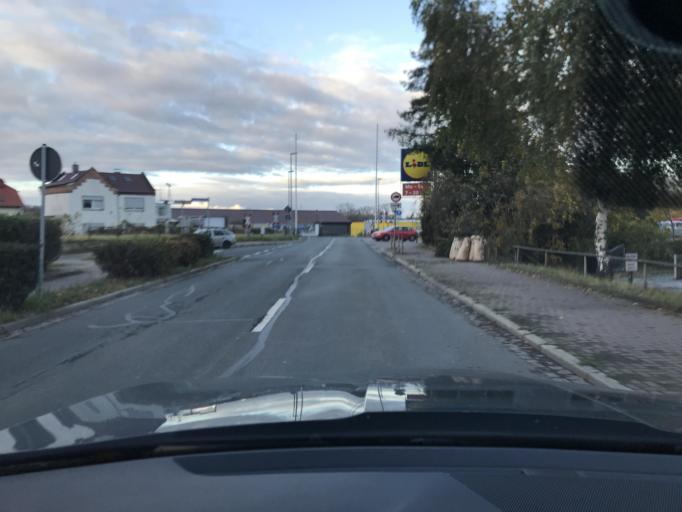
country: DE
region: Saxony-Anhalt
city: Thale
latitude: 51.7497
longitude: 11.0408
